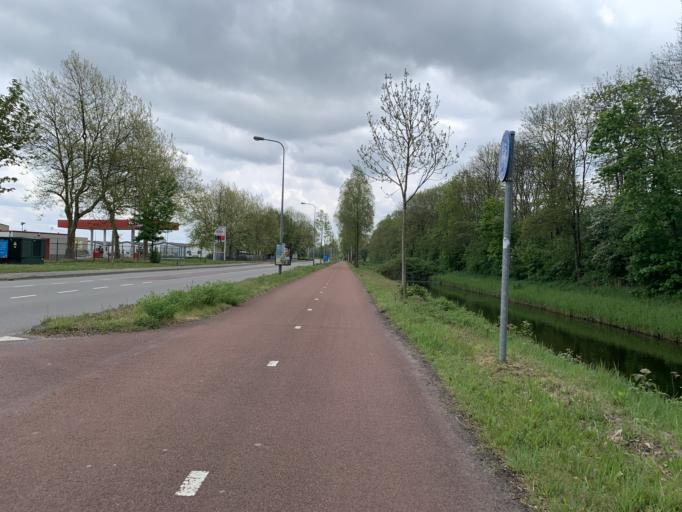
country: NL
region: Groningen
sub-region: Gemeente Groningen
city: Oosterpark
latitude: 53.2063
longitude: 6.5978
